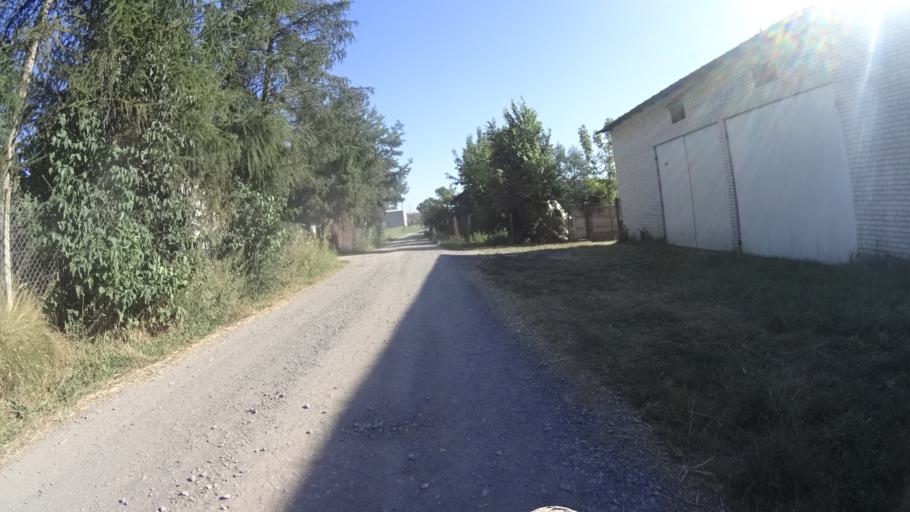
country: PL
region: Masovian Voivodeship
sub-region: Powiat bialobrzeski
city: Wysmierzyce
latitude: 51.6675
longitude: 20.8492
